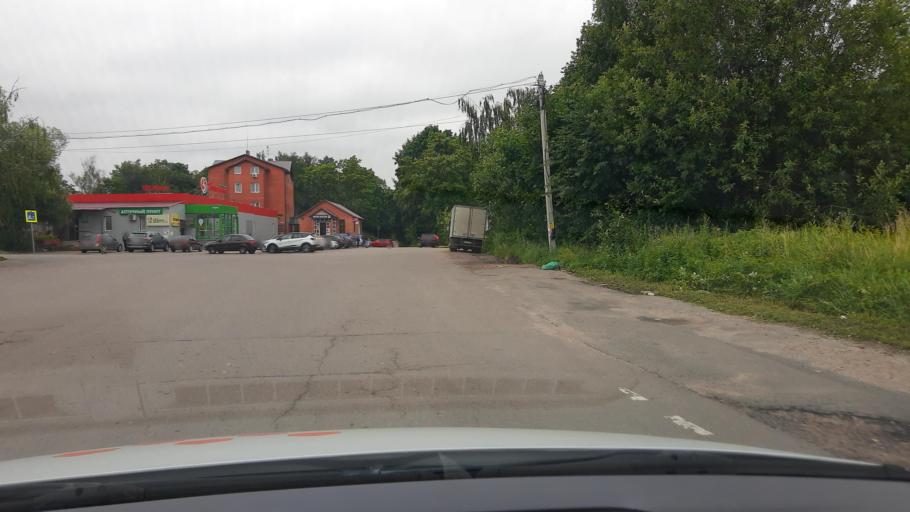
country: RU
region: Moskovskaya
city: Gorki-Leninskiye
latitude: 55.4973
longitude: 37.8252
